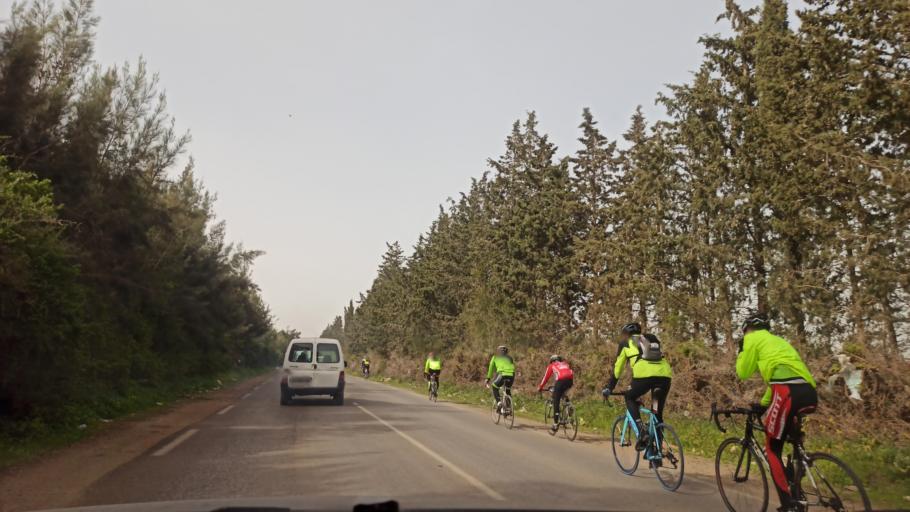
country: TN
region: Zaghwan
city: Zaghouan
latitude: 36.4185
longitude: 10.1092
